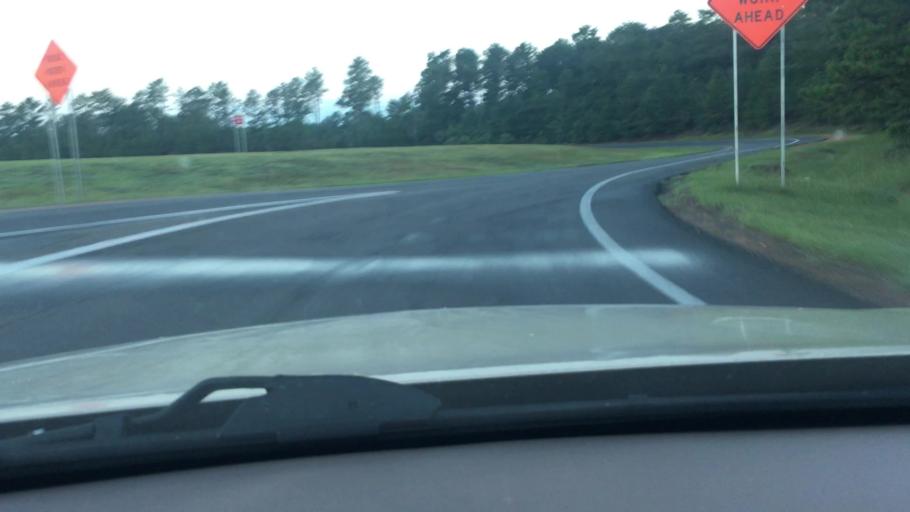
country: US
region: South Carolina
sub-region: Lexington County
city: Irmo
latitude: 34.0993
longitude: -81.1730
